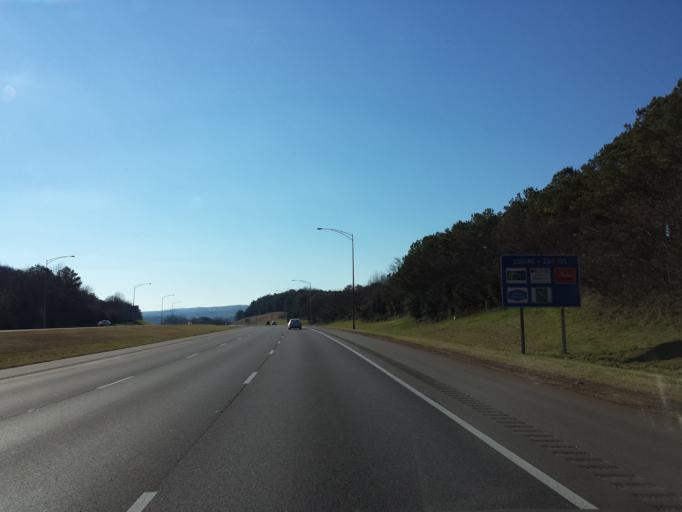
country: US
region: Alabama
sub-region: Jefferson County
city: Irondale
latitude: 33.5432
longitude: -86.6810
